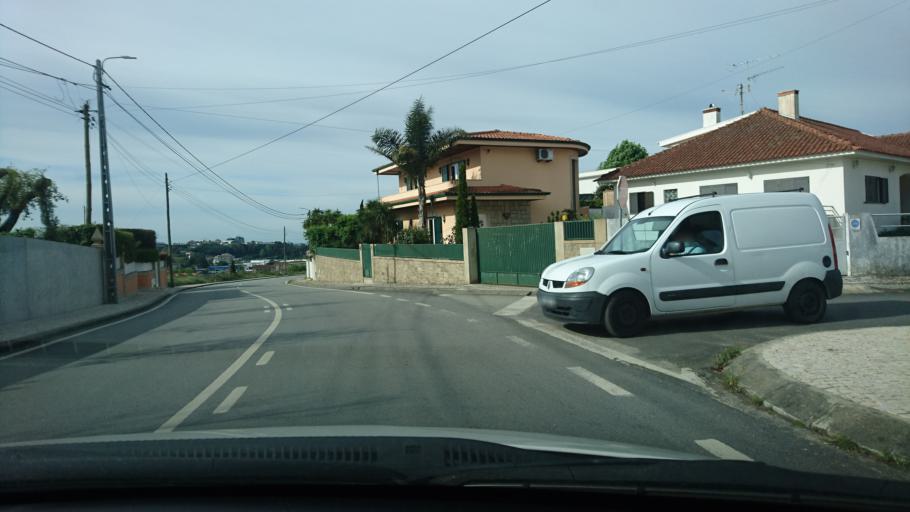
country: PT
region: Aveiro
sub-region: Oliveira de Azemeis
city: Vila Cha
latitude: 40.8586
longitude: -8.4743
